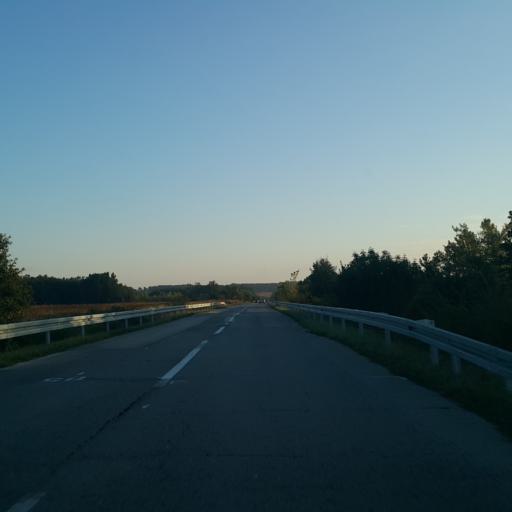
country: RS
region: Central Serbia
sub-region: Borski Okrug
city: Negotin
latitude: 44.1421
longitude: 22.3505
